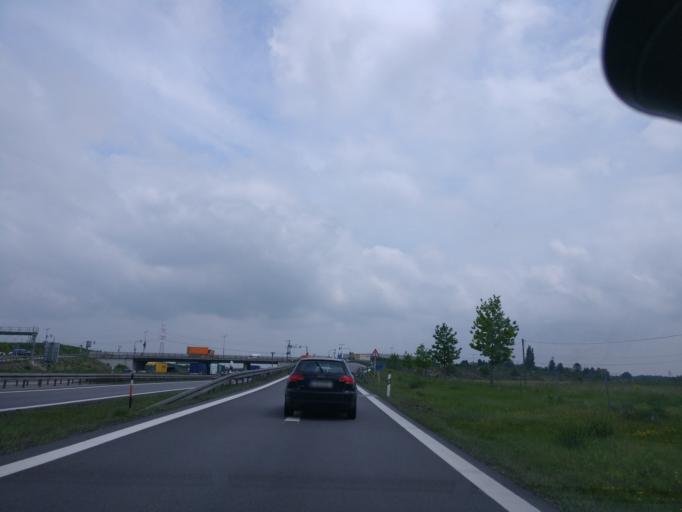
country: DE
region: Bavaria
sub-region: Upper Bavaria
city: Pasing
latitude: 48.1727
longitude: 11.4232
